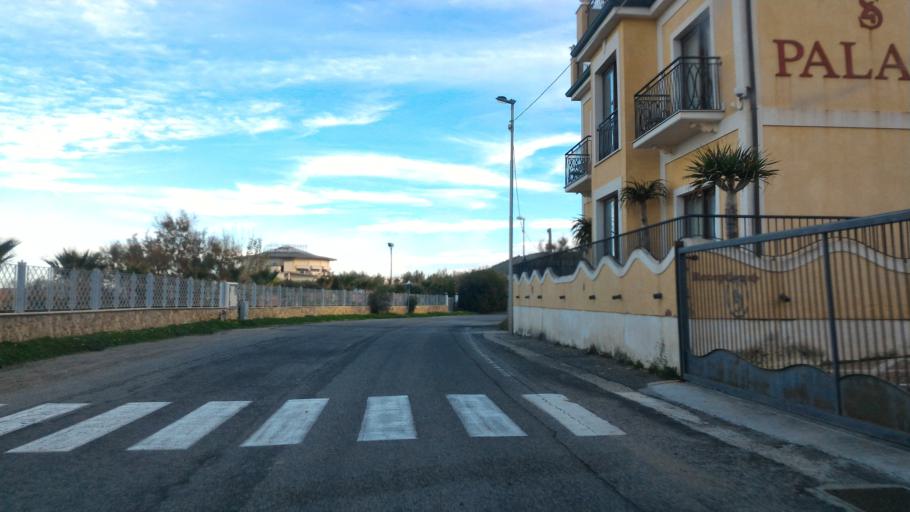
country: IT
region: Calabria
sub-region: Provincia di Crotone
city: Crotone
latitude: 39.0493
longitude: 17.1435
